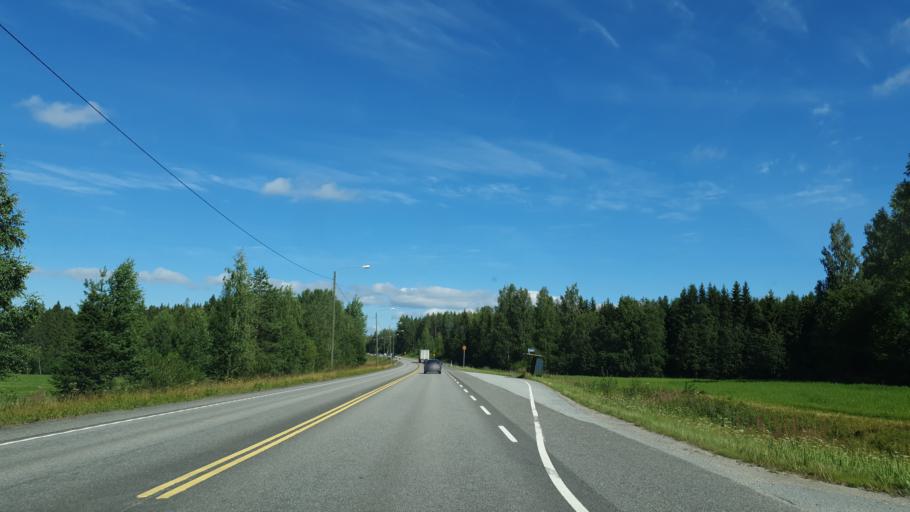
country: FI
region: Central Finland
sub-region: Jyvaeskylae
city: Toivakka
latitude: 62.2451
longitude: 25.9960
